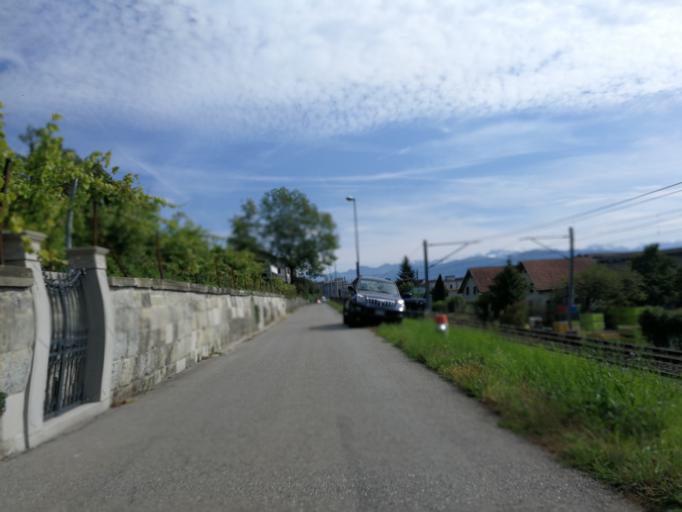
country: CH
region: Zurich
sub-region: Bezirk Meilen
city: Obermeilen
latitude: 47.2621
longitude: 8.6698
